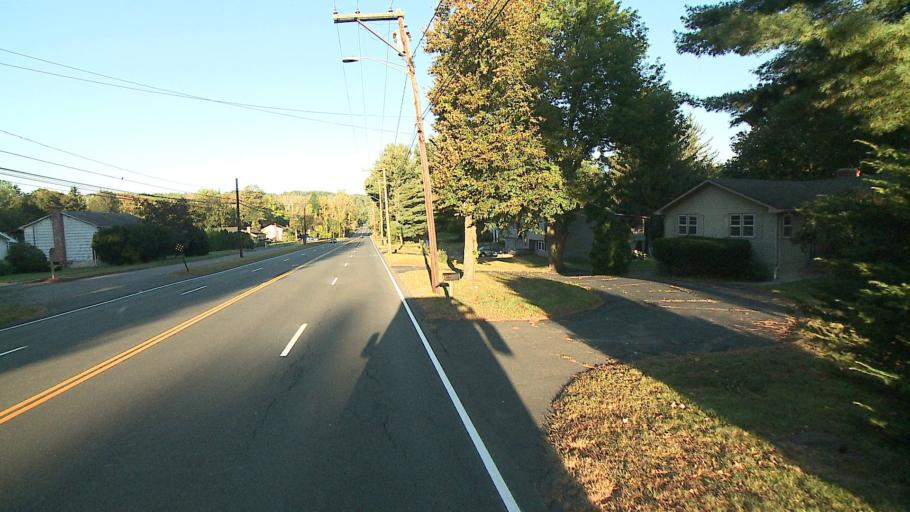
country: US
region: Connecticut
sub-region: Hartford County
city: West Hartford
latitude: 41.7867
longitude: -72.7587
